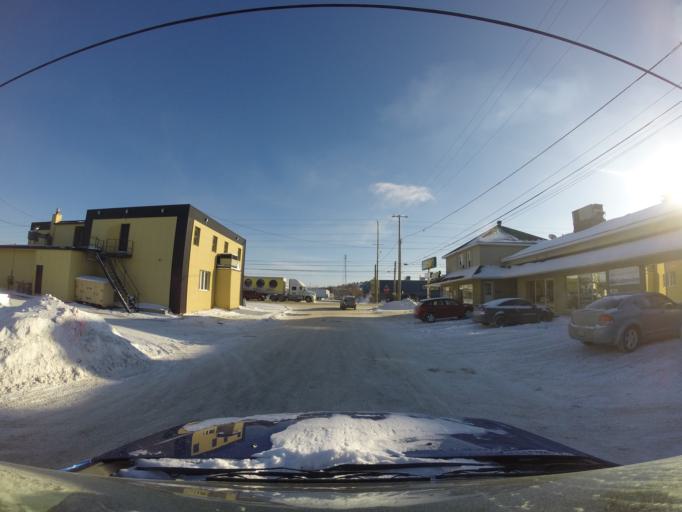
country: CA
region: Ontario
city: Greater Sudbury
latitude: 46.4765
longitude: -81.0209
